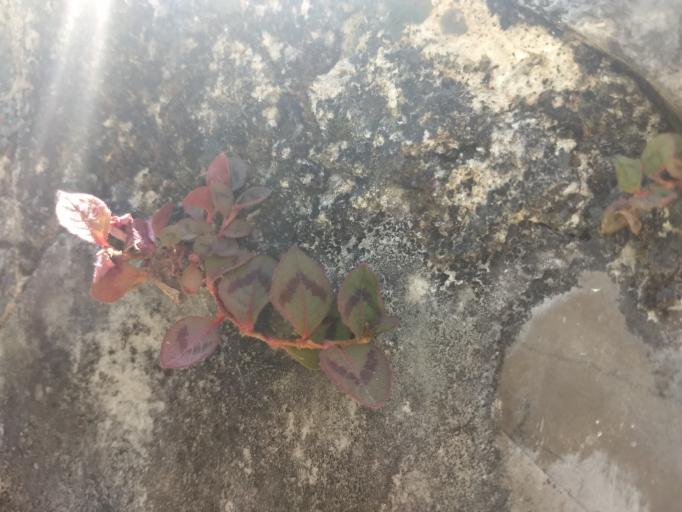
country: MX
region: Puebla
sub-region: Cuetzalan del Progreso
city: Ciudad de Cuetzalan
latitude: 20.0128
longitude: -97.5052
